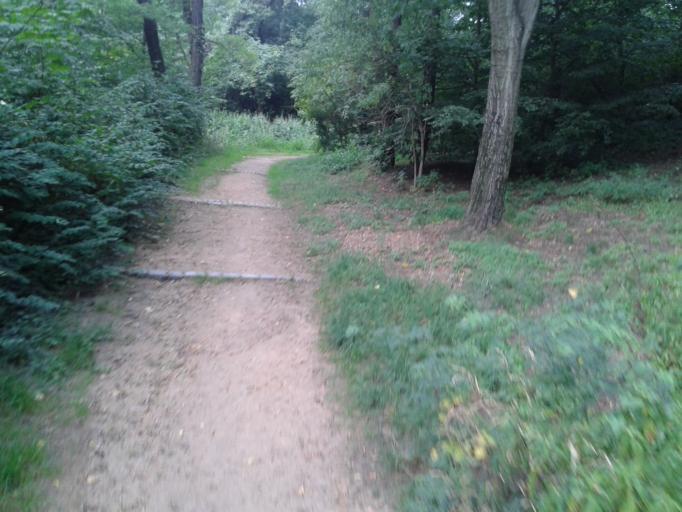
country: DE
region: Saxony
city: Albertstadt
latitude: 51.0803
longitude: 13.7474
